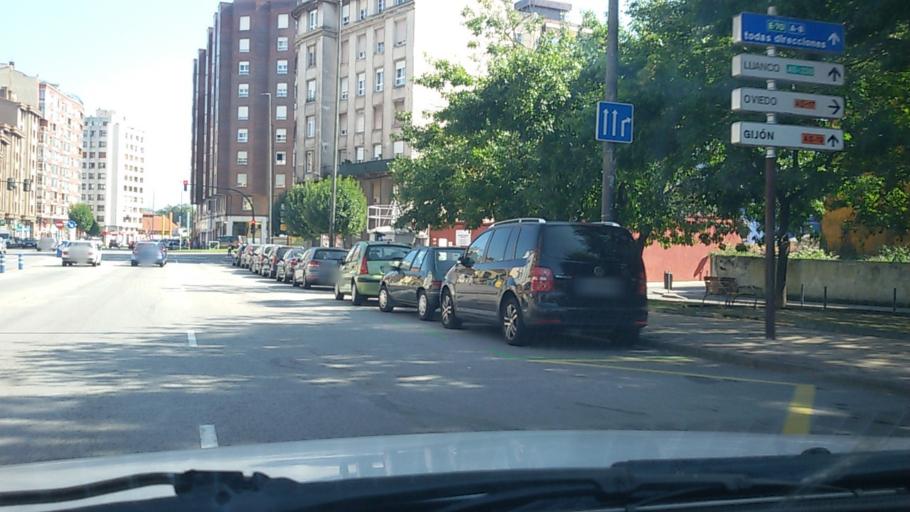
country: ES
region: Asturias
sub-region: Province of Asturias
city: Aviles
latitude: 43.5510
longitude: -5.9201
